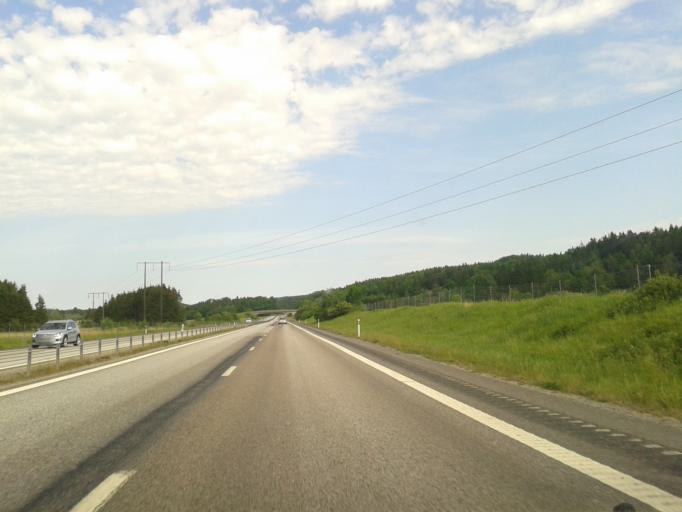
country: SE
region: Vaestra Goetaland
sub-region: Munkedals Kommun
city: Munkedal
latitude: 58.5314
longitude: 11.5380
